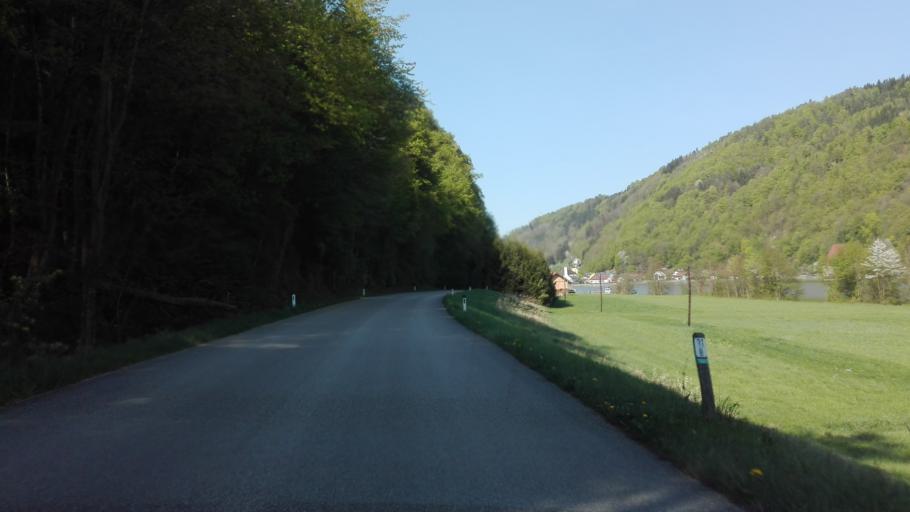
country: AT
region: Upper Austria
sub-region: Politischer Bezirk Rohrbach
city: Atzesberg
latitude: 48.4428
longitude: 13.9175
